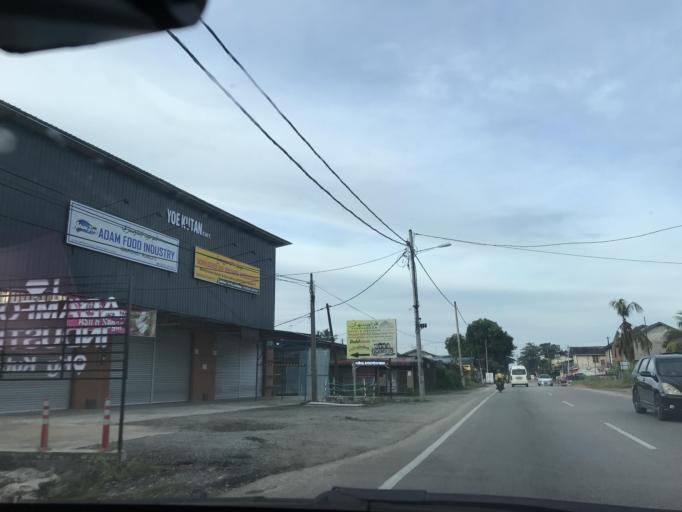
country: MY
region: Kelantan
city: Kota Bharu
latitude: 6.1049
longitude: 102.2116
